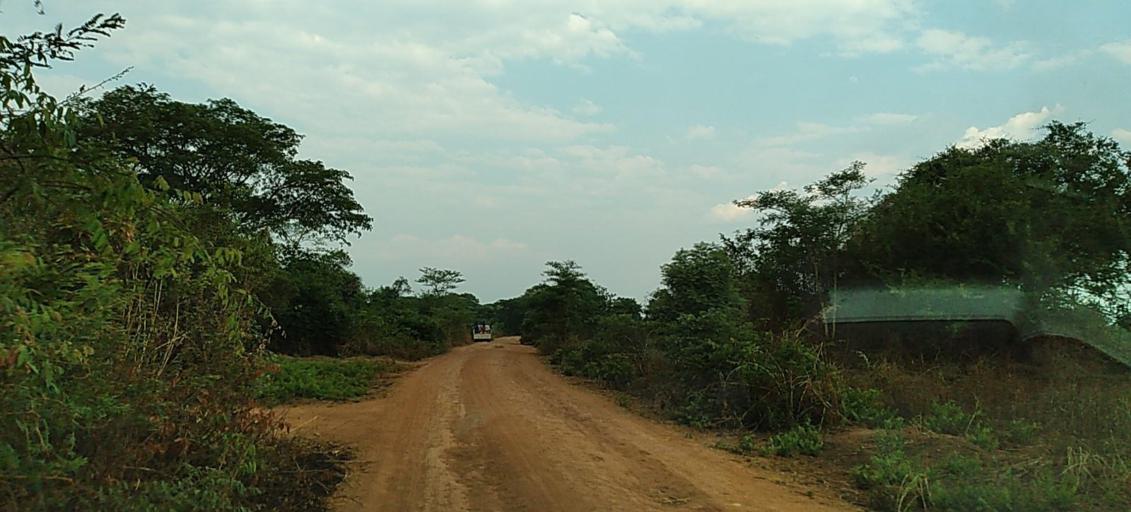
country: ZM
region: Copperbelt
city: Kalulushi
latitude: -13.0183
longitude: 27.9165
